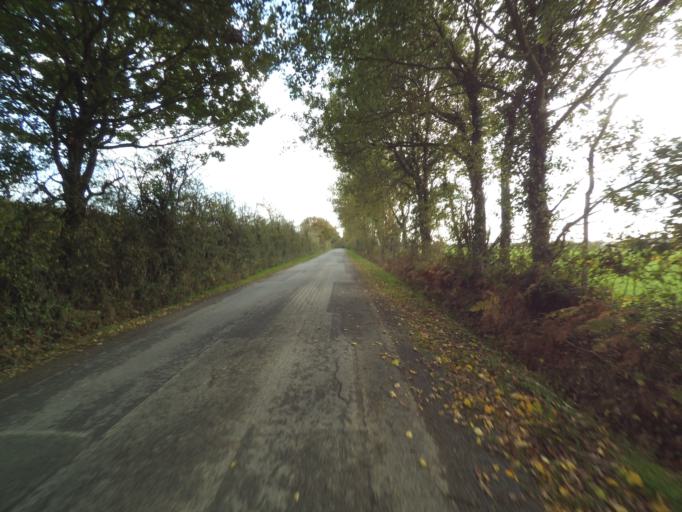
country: FR
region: Pays de la Loire
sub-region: Departement de la Vendee
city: Saint-Hilaire-de-Loulay
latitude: 47.0195
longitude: -1.3555
